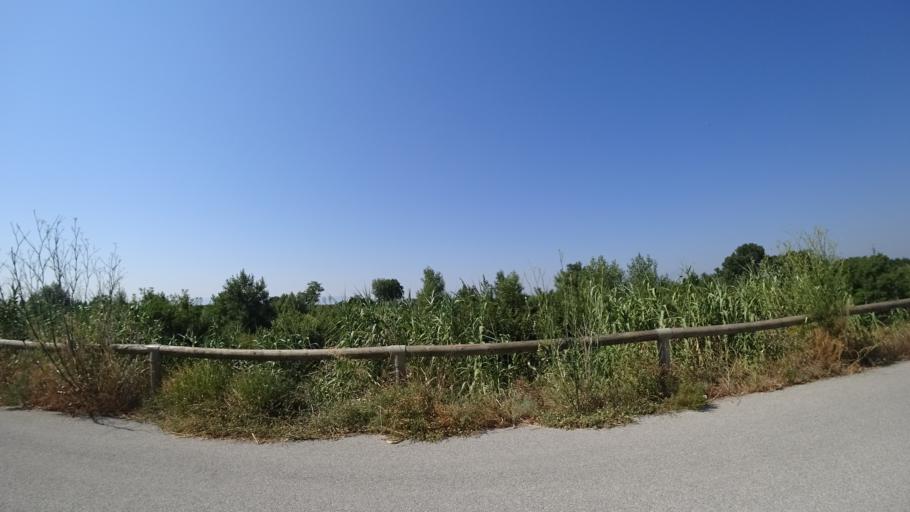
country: FR
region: Languedoc-Roussillon
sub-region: Departement des Pyrenees-Orientales
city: Pia
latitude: 42.7619
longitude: 2.9159
